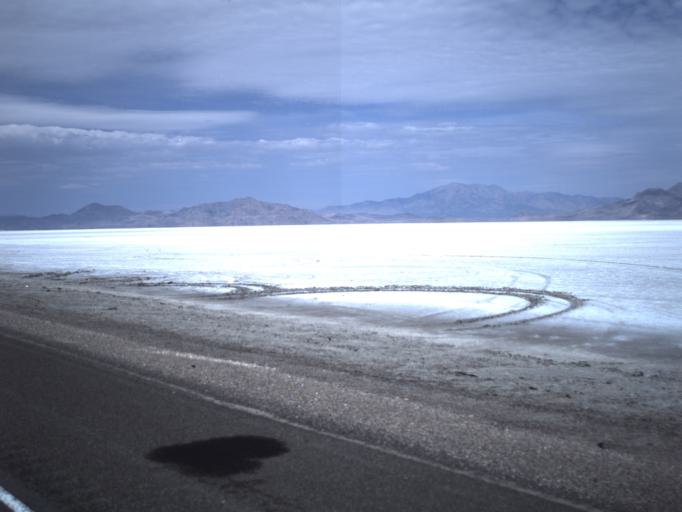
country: US
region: Utah
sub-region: Tooele County
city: Wendover
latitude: 40.7365
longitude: -113.7089
